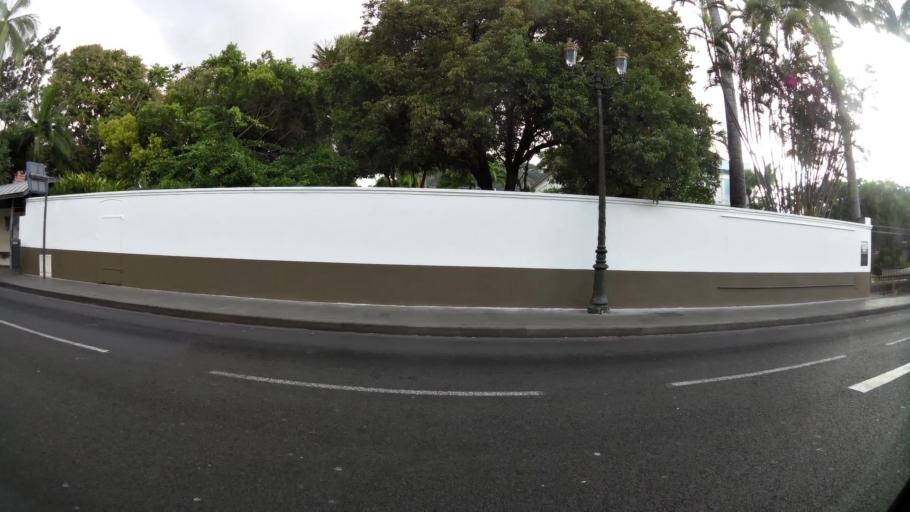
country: RE
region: Reunion
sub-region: Reunion
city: Saint-Denis
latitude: -20.8817
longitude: 55.4496
